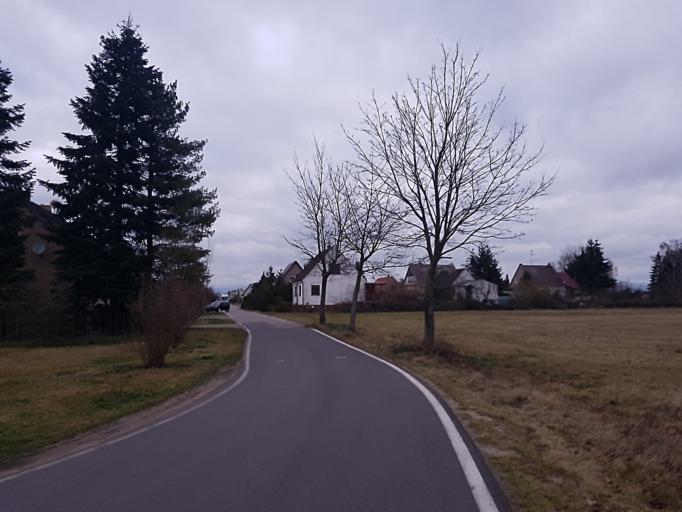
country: DE
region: Brandenburg
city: Falkenberg
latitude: 51.5865
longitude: 13.2923
